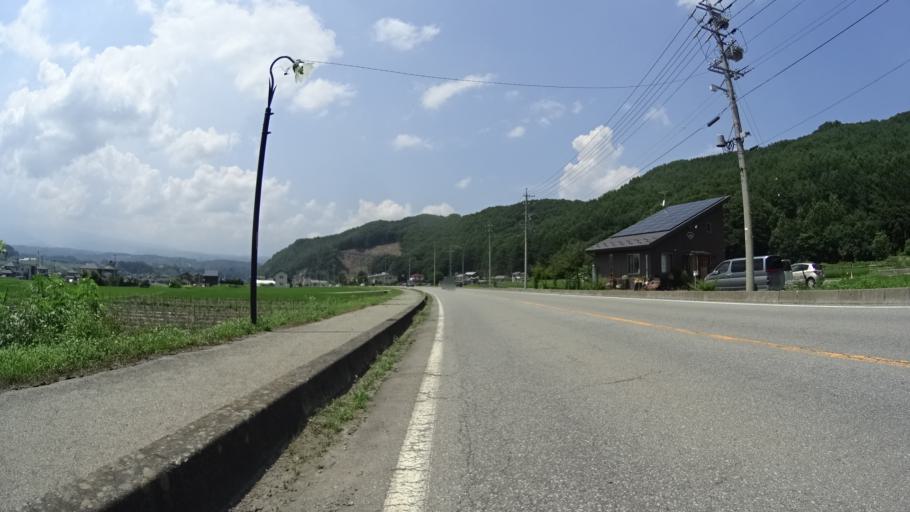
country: JP
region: Nagano
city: Saku
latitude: 36.1536
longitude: 138.5038
